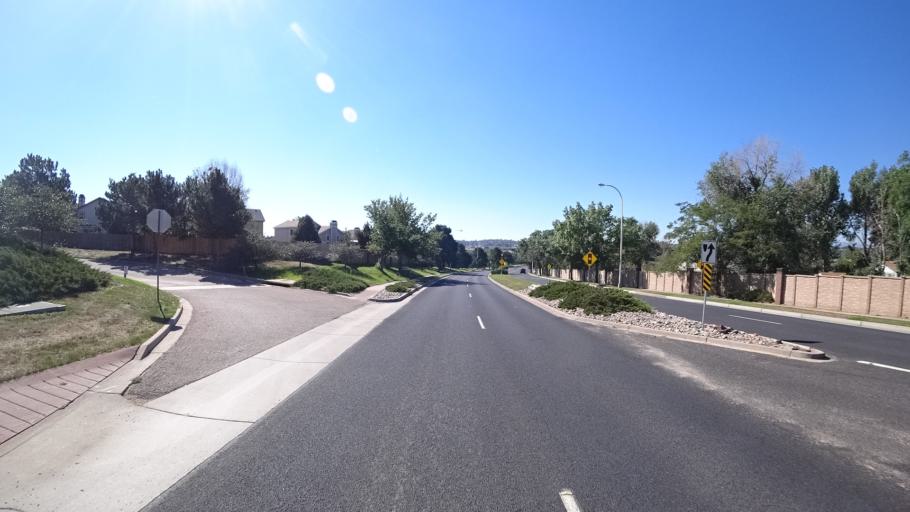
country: US
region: Colorado
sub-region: El Paso County
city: Cimarron Hills
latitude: 38.9344
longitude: -104.7547
